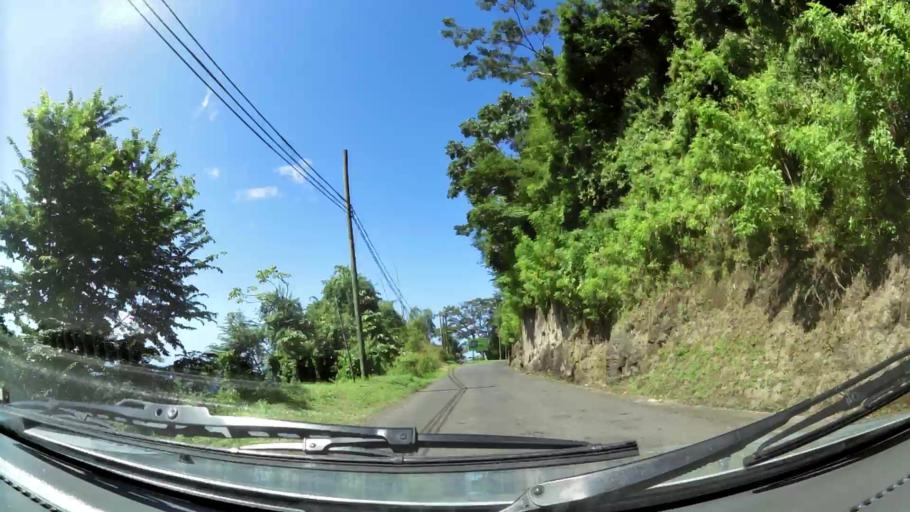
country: GD
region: Saint John
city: Gouyave
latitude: 12.1211
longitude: -61.7440
